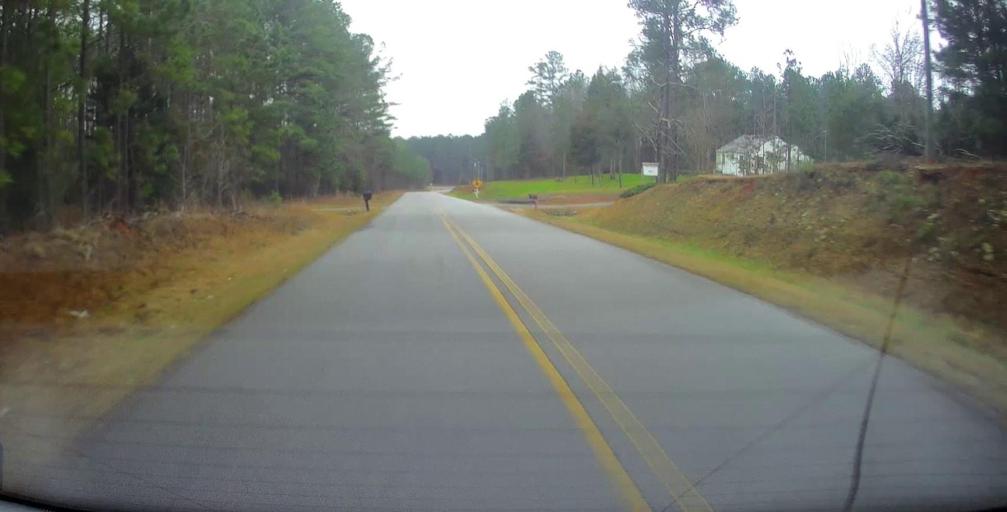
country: US
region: Georgia
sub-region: Monroe County
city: Forsyth
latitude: 33.0822
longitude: -83.9130
